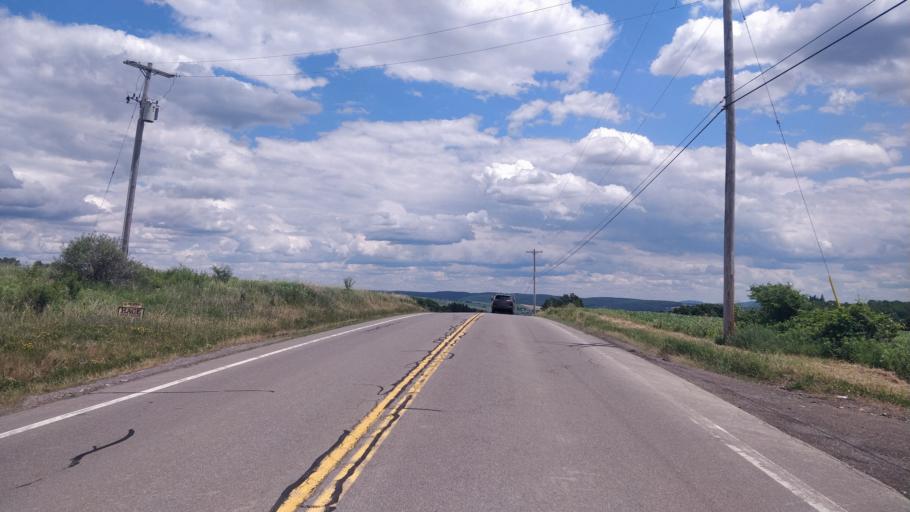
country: US
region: New York
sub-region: Cortland County
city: Homer
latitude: 42.6400
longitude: -76.2235
